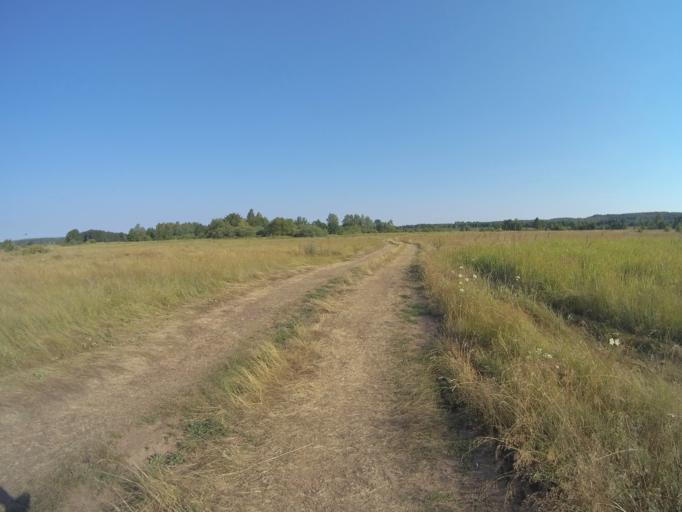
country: RU
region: Vladimir
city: Vorsha
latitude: 56.0282
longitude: 40.1970
